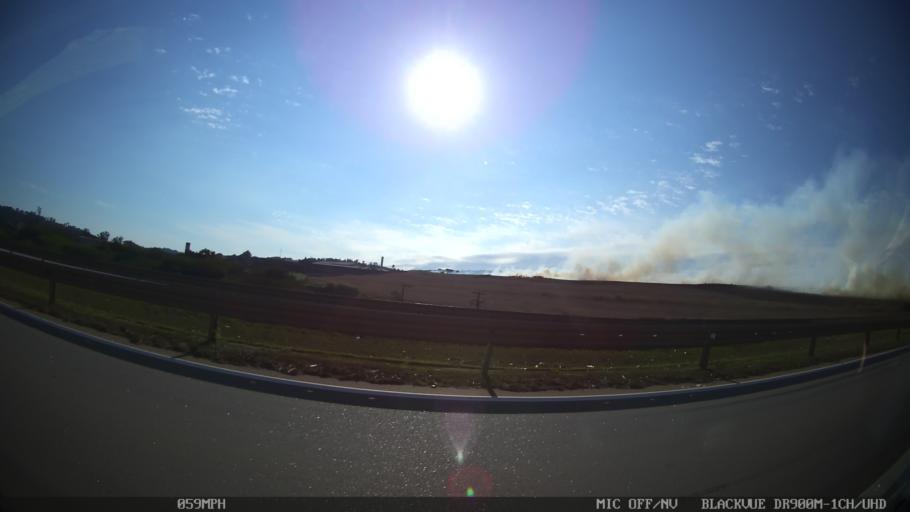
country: BR
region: Sao Paulo
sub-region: Piracicaba
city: Piracicaba
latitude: -22.6997
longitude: -47.6080
